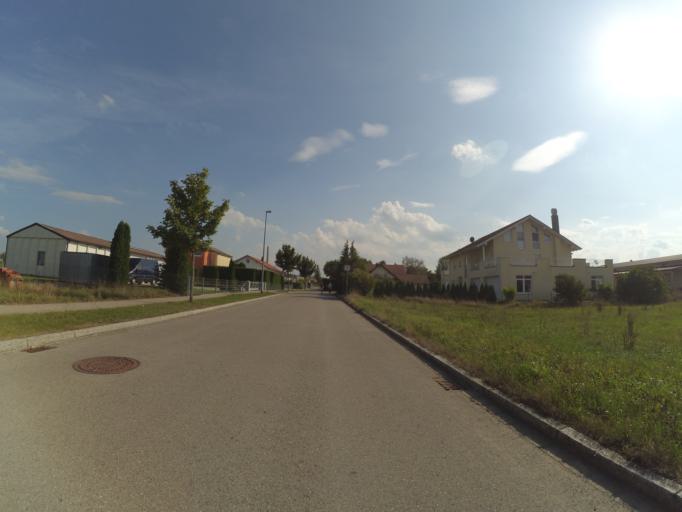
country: DE
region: Bavaria
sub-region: Swabia
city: Buchloe
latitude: 48.0414
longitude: 10.7131
